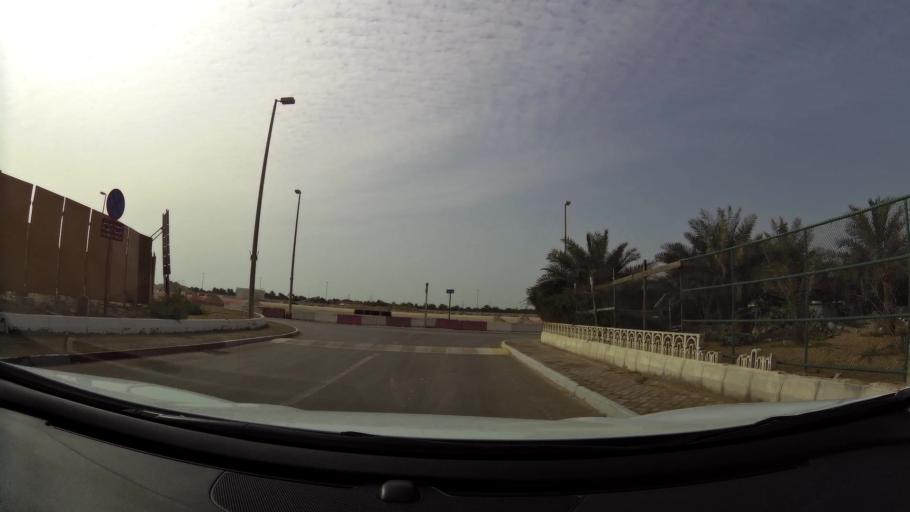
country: AE
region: Abu Dhabi
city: Abu Dhabi
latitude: 24.5949
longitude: 54.6946
